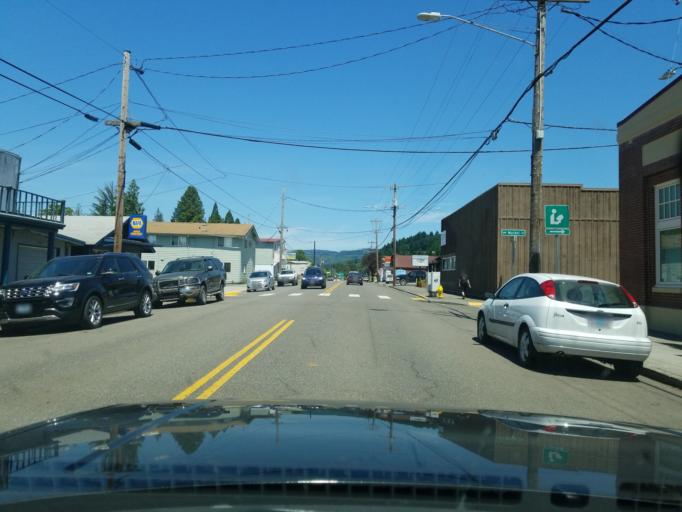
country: US
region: Oregon
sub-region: Washington County
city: Banks
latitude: 45.6195
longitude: -123.1144
